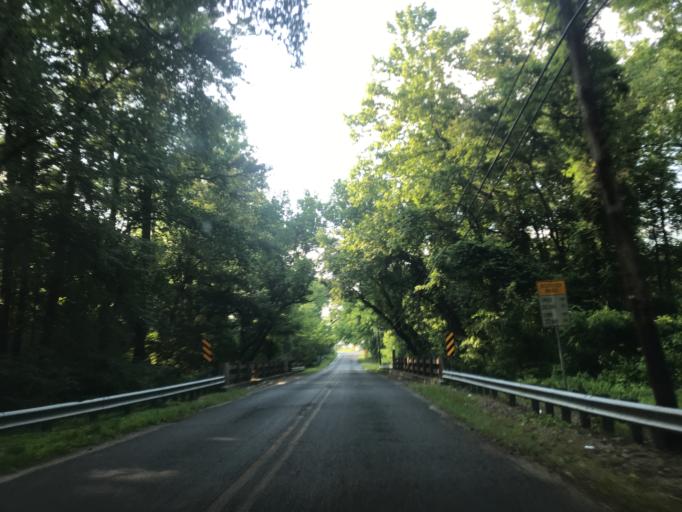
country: US
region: Maryland
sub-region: Caroline County
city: Federalsburg
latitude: 38.7100
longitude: -75.7762
